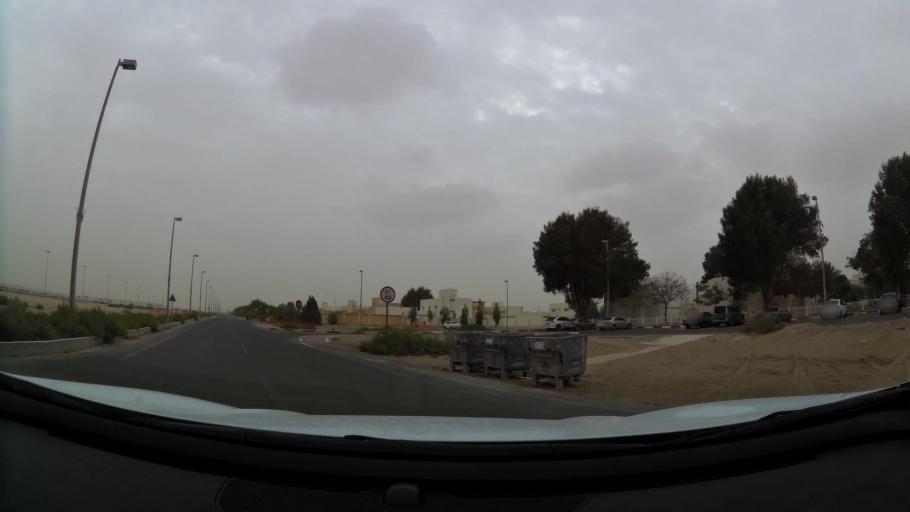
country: AE
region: Abu Dhabi
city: Abu Dhabi
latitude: 24.4262
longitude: 54.7208
